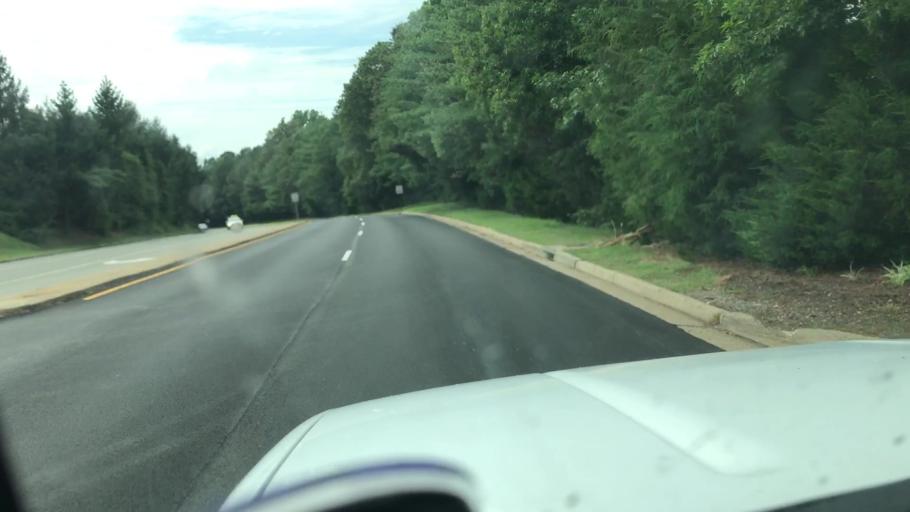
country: US
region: Virginia
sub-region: Henrico County
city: Short Pump
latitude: 37.6249
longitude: -77.5945
